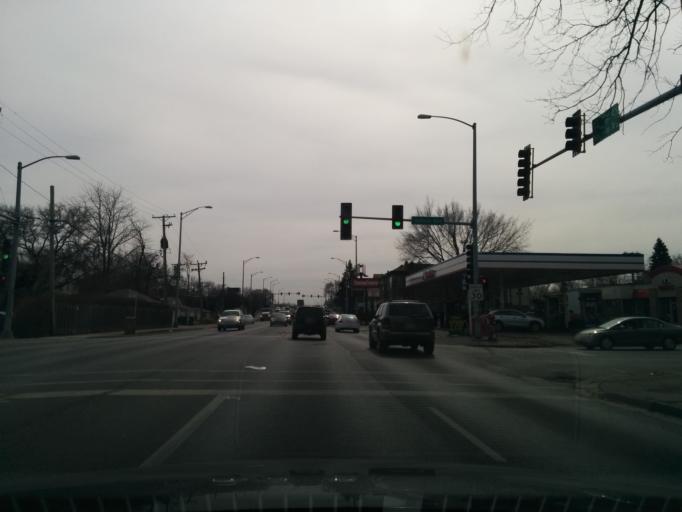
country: US
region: Illinois
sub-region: Cook County
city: Forest Park
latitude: 41.8762
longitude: -87.8046
